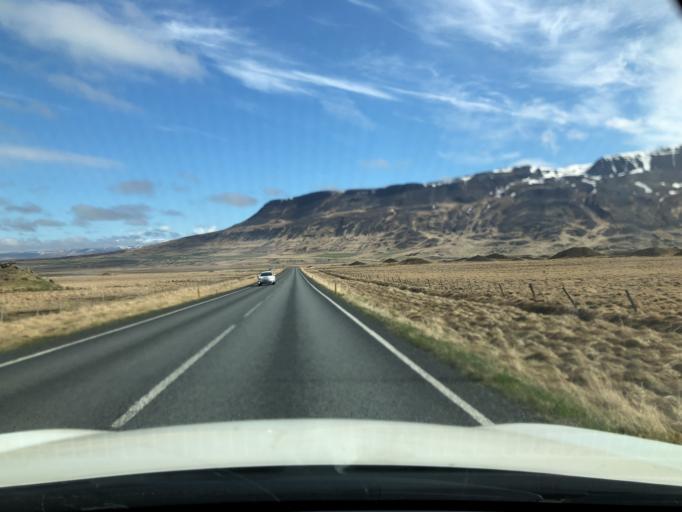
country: IS
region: Northwest
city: Saudarkrokur
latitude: 65.5014
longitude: -20.3968
